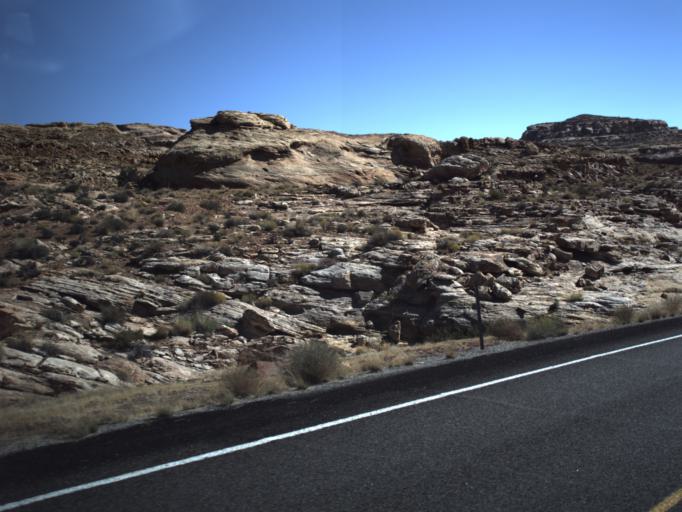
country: US
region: Utah
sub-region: San Juan County
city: Blanding
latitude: 37.8936
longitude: -110.3723
